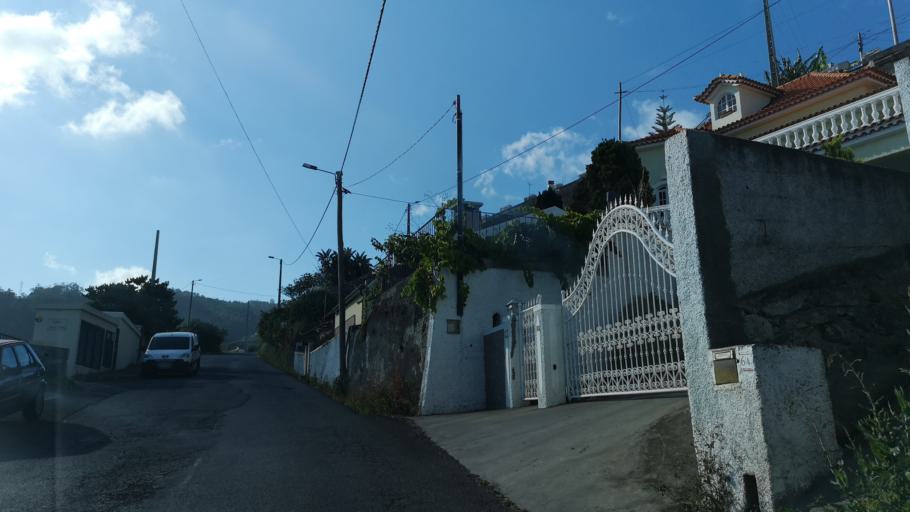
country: PT
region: Madeira
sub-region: Santa Cruz
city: Camacha
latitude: 32.6581
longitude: -16.8380
